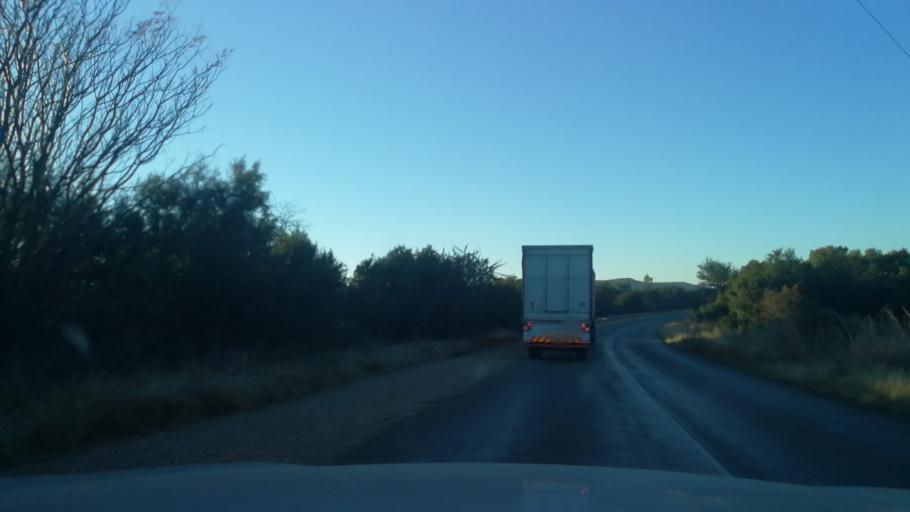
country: ZA
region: North-West
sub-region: Bojanala Platinum District Municipality
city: Koster
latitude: -25.6544
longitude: 26.7121
